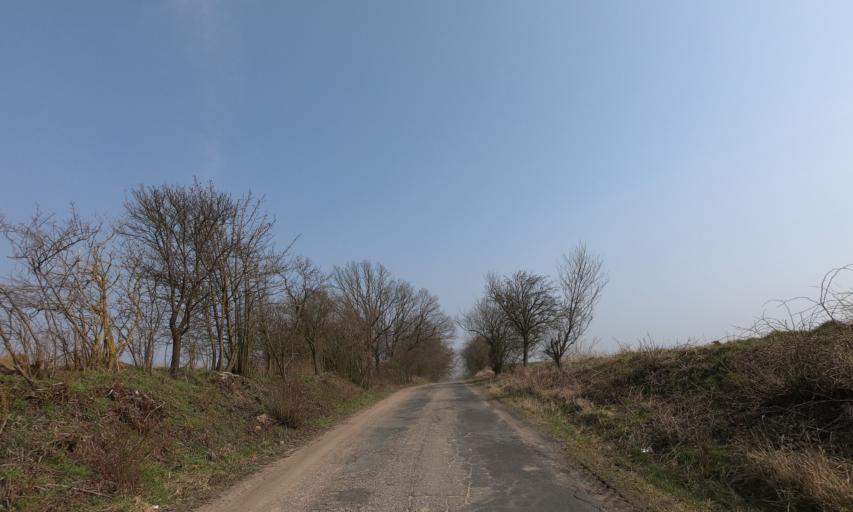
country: PL
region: West Pomeranian Voivodeship
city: Trzcinsko Zdroj
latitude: 52.9408
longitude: 14.7089
